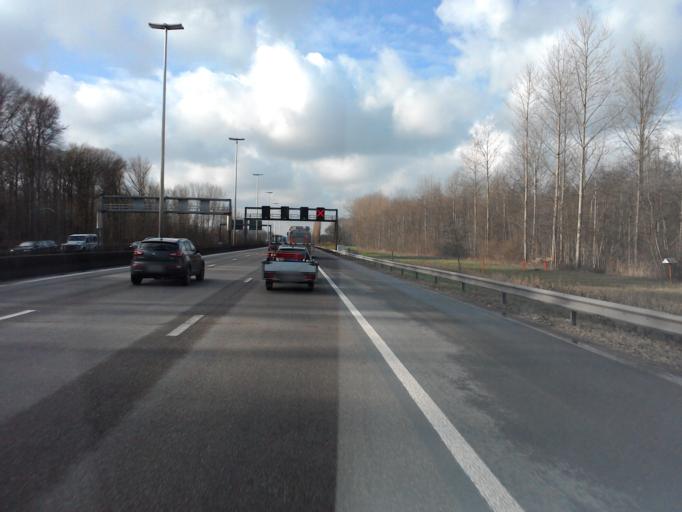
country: BE
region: Flanders
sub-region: Provincie Antwerpen
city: Ranst
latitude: 51.2039
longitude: 4.5678
